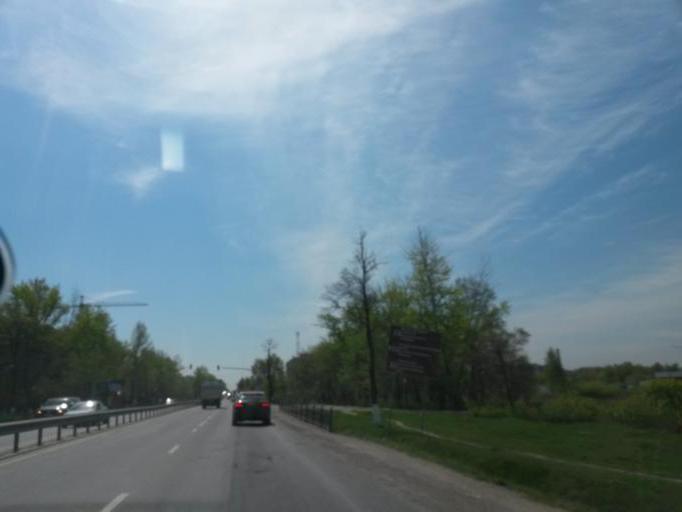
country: RU
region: Moskovskaya
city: Shcherbinka
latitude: 55.4848
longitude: 37.5664
